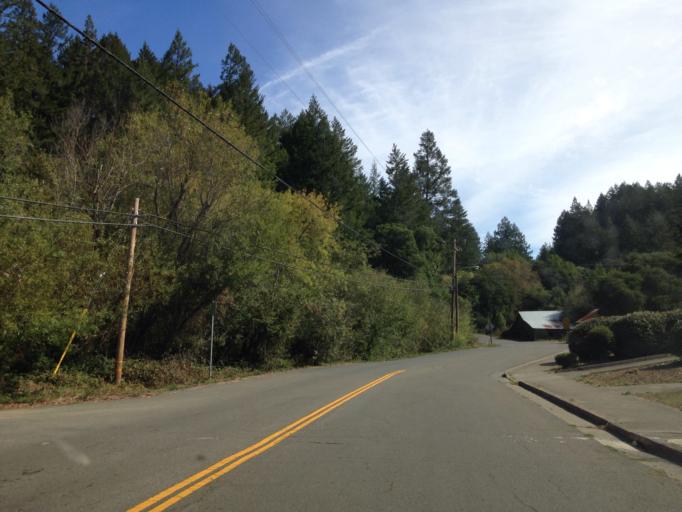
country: US
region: California
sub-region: Sonoma County
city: Occidental
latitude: 38.4104
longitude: -122.9491
